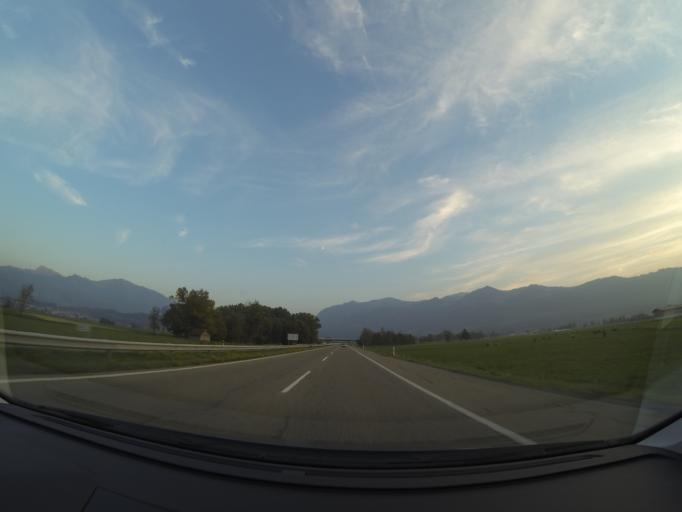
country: CH
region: Schwyz
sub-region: Bezirk March
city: Tuggen
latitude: 47.2048
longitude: 8.9655
